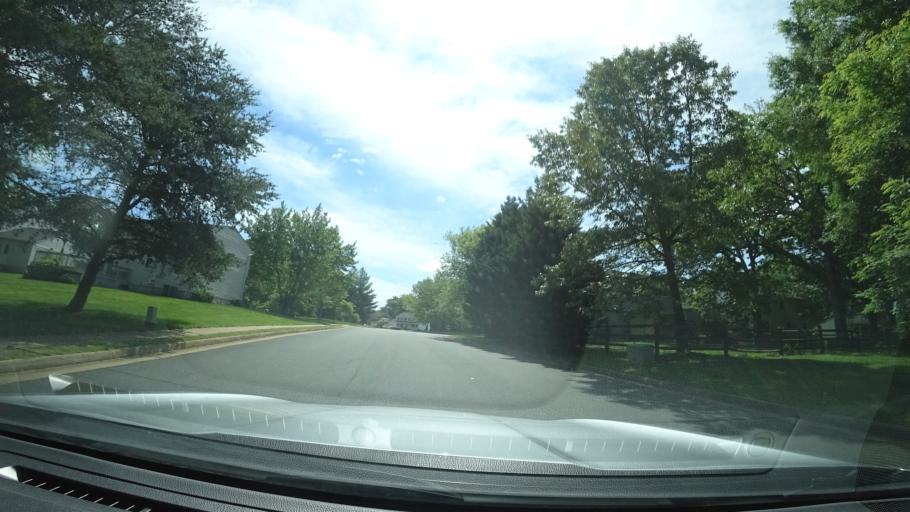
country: US
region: Virginia
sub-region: Loudoun County
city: Oak Grove
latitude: 38.9875
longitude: -77.4037
